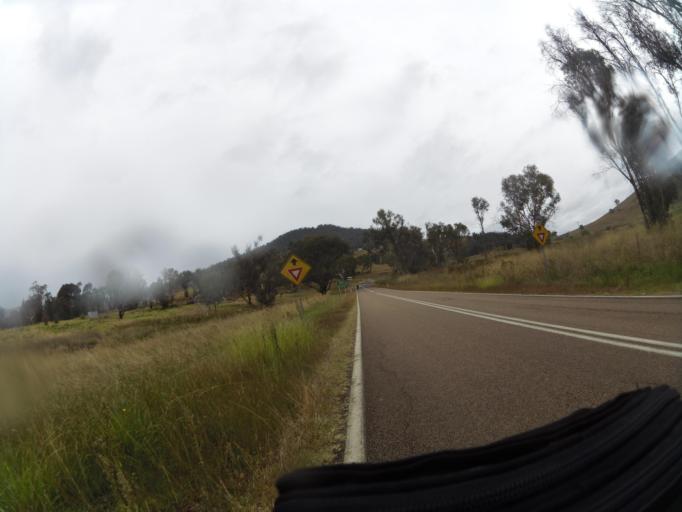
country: AU
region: New South Wales
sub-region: Greater Hume Shire
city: Holbrook
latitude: -36.2192
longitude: 147.7299
